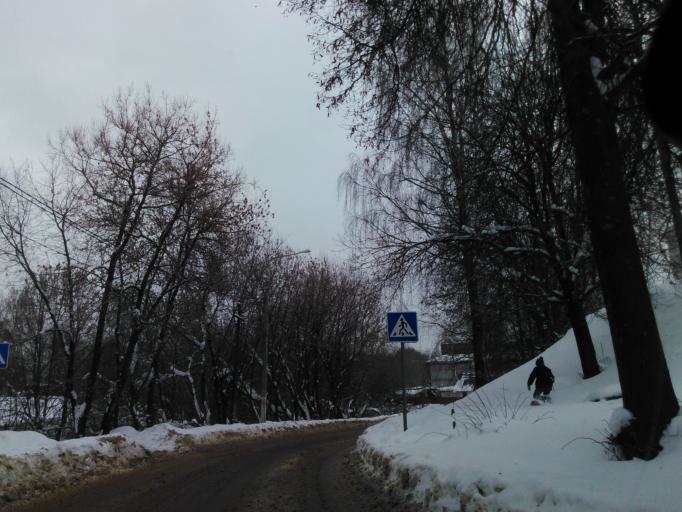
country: RU
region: Moskovskaya
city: Yakhroma
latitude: 56.2862
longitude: 37.4818
